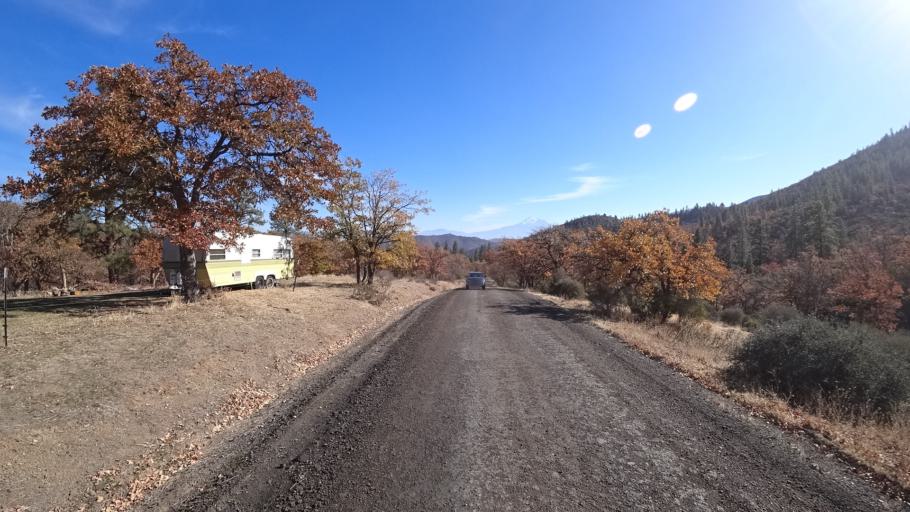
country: US
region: California
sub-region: Siskiyou County
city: Yreka
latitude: 41.7753
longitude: -122.6512
